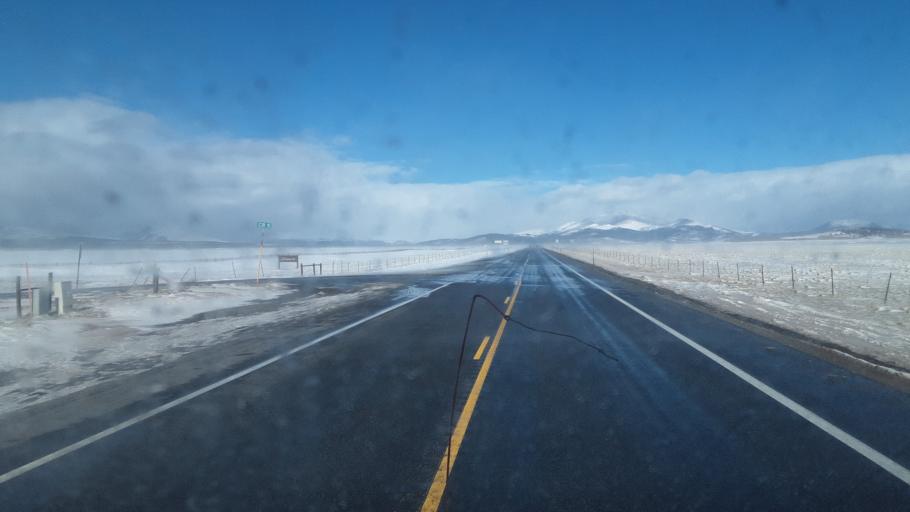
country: US
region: Colorado
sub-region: Park County
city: Fairplay
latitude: 39.1532
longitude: -105.9990
